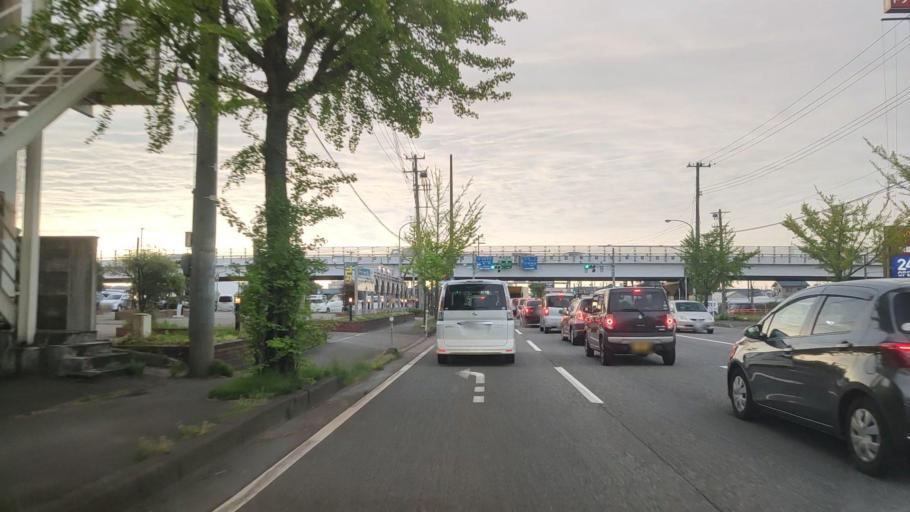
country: JP
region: Niigata
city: Kameda-honcho
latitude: 37.9114
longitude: 139.0985
